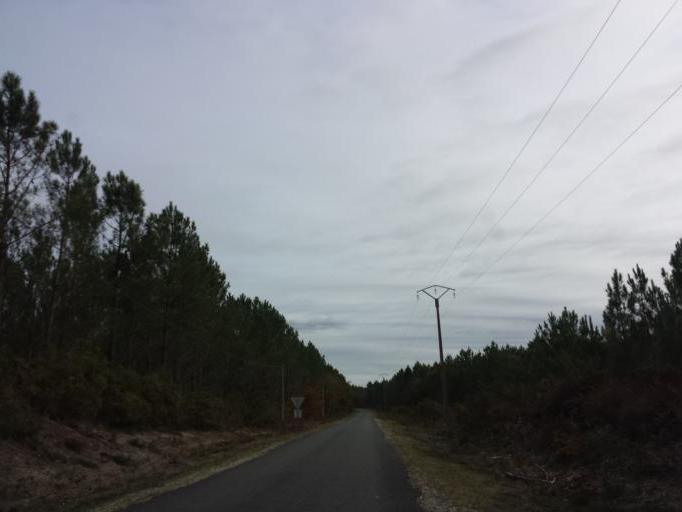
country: FR
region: Aquitaine
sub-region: Departement de la Gironde
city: Lacanau
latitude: 44.9489
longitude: -1.0652
